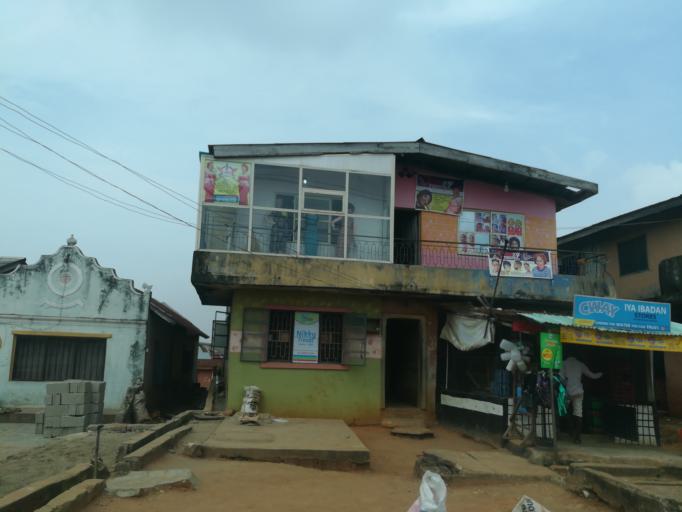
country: NG
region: Lagos
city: Ikorodu
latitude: 6.6120
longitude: 3.5049
